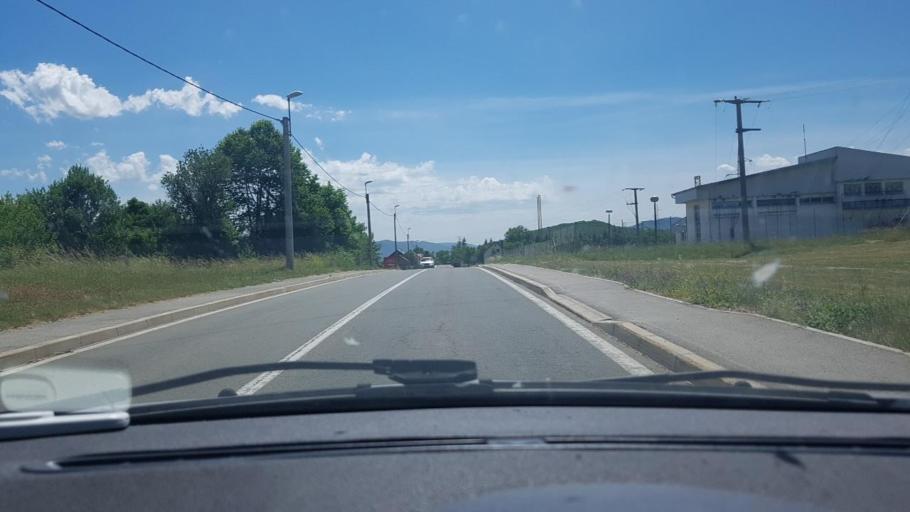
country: HR
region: Licko-Senjska
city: Otocac
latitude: 44.8640
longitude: 15.2596
